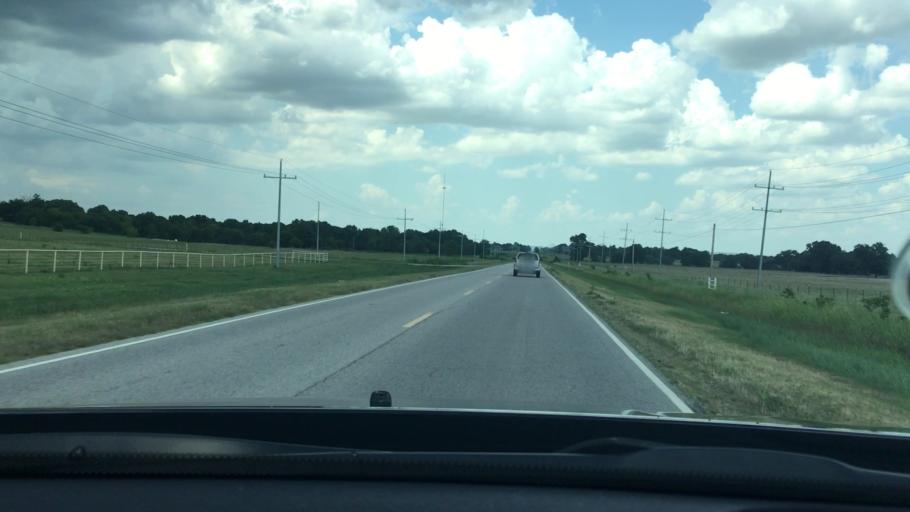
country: US
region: Oklahoma
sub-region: Pontotoc County
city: Ada
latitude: 34.6412
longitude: -96.6348
